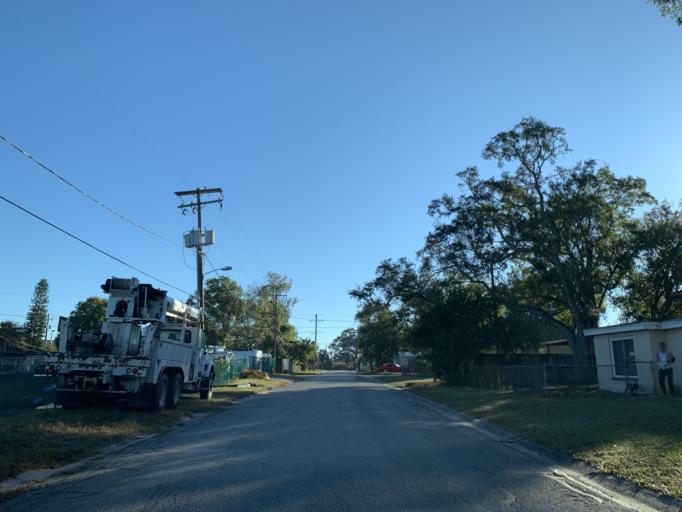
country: US
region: Florida
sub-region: Hillsborough County
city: University
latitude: 28.0411
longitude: -82.4281
